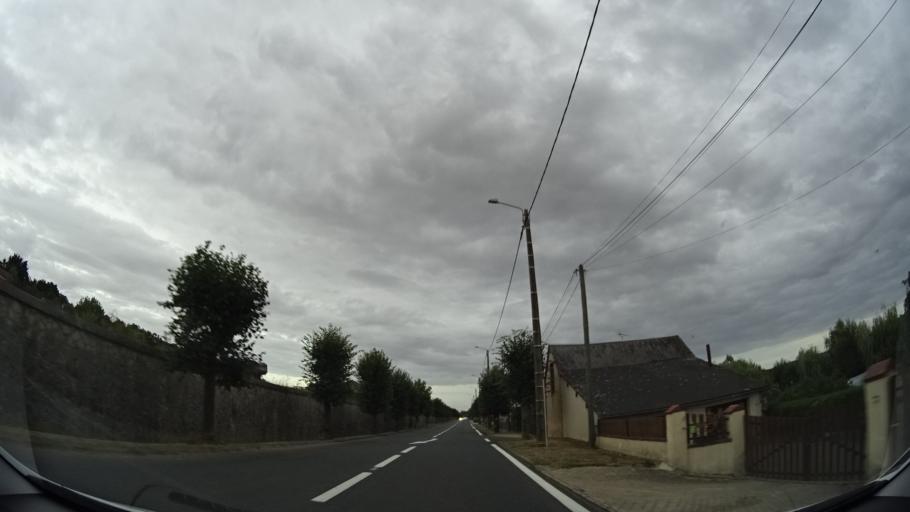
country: FR
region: Centre
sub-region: Departement du Loiret
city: Trigueres
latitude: 47.9393
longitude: 2.9758
